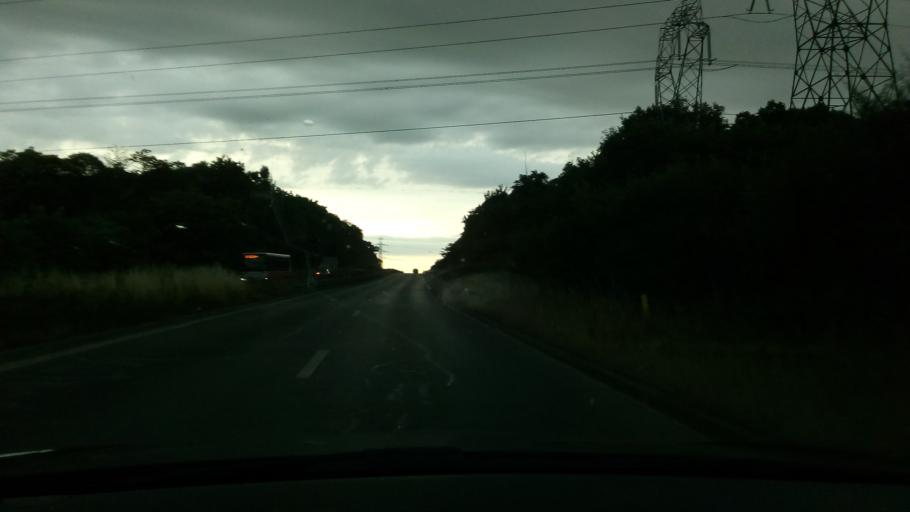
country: FR
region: Ile-de-France
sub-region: Departement de Seine-et-Marne
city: Voisenon
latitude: 48.5606
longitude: 2.6459
